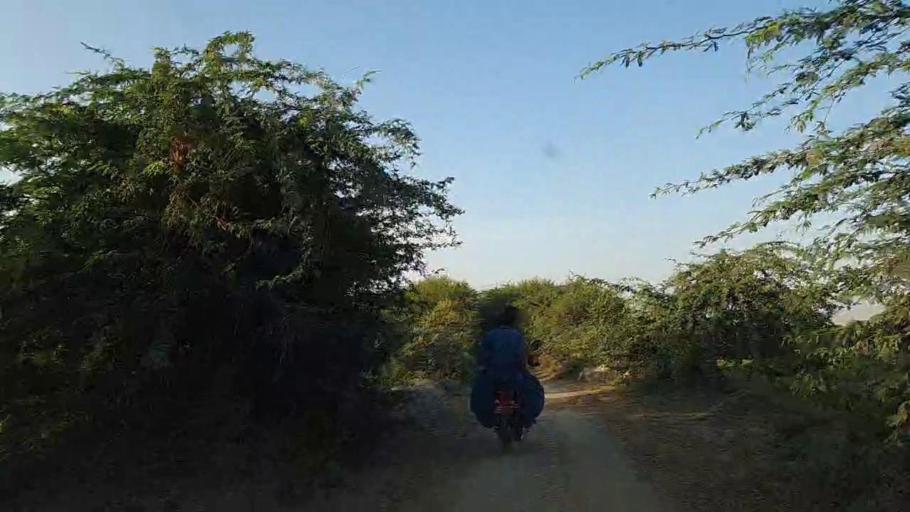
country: PK
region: Sindh
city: Mirpur Batoro
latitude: 24.7167
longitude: 68.2146
